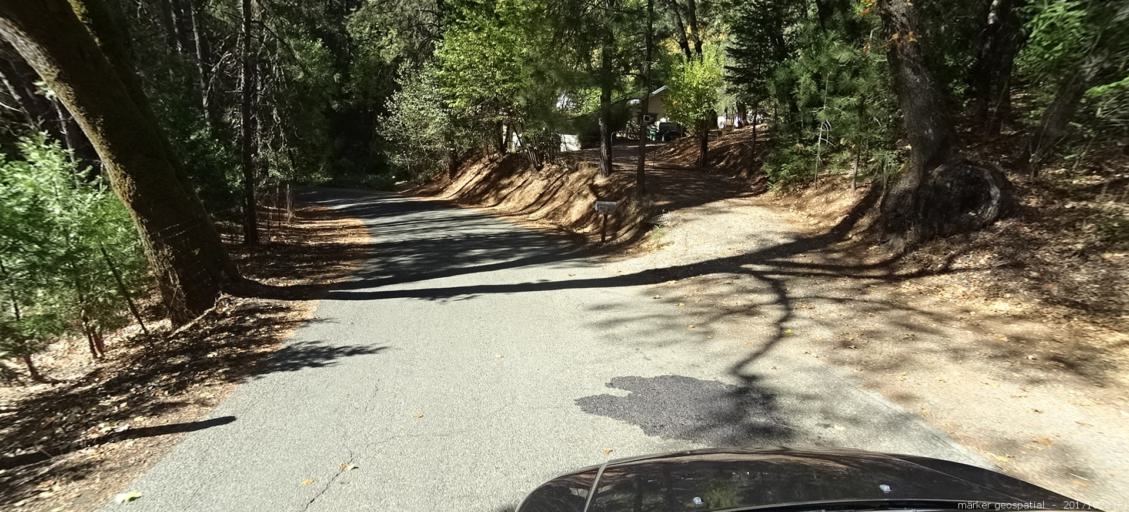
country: US
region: California
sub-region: Shasta County
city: Central Valley (historical)
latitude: 40.9396
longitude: -122.4491
